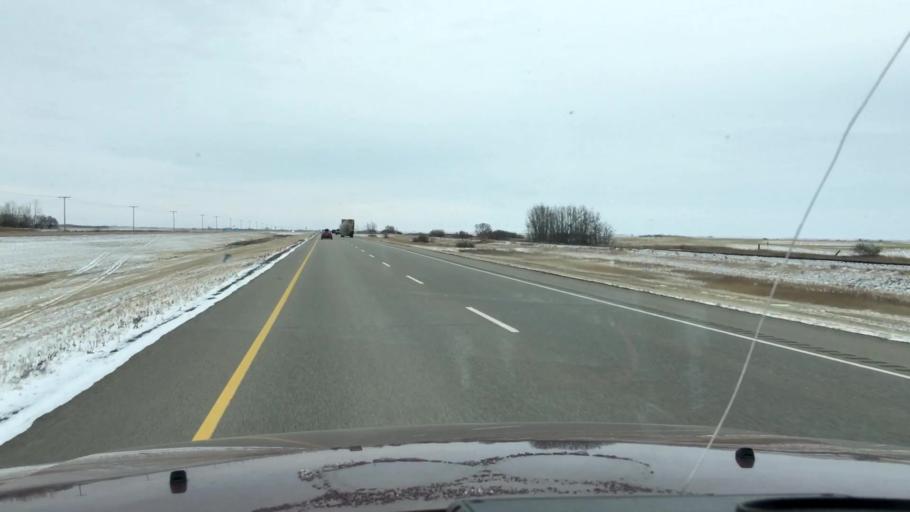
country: CA
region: Saskatchewan
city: Watrous
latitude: 51.1949
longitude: -105.9524
